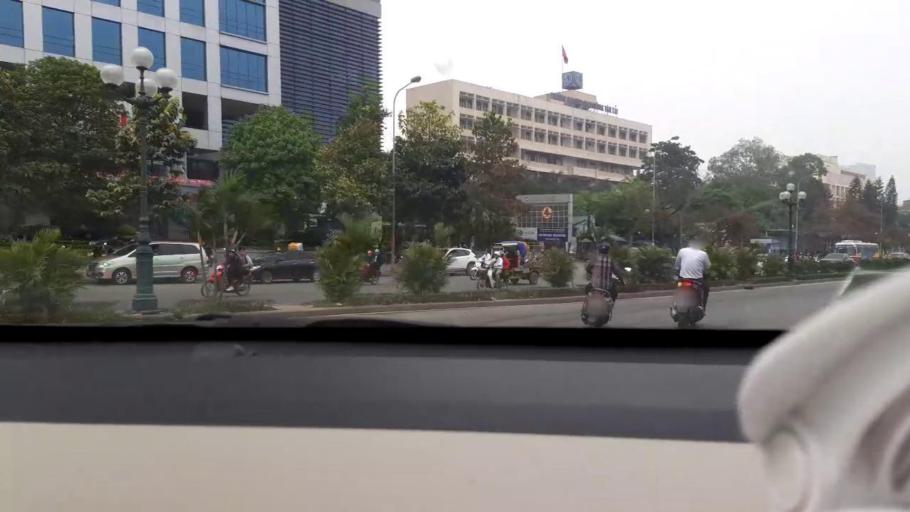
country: VN
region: Ha Noi
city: Cau Giay
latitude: 21.0283
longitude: 105.8049
